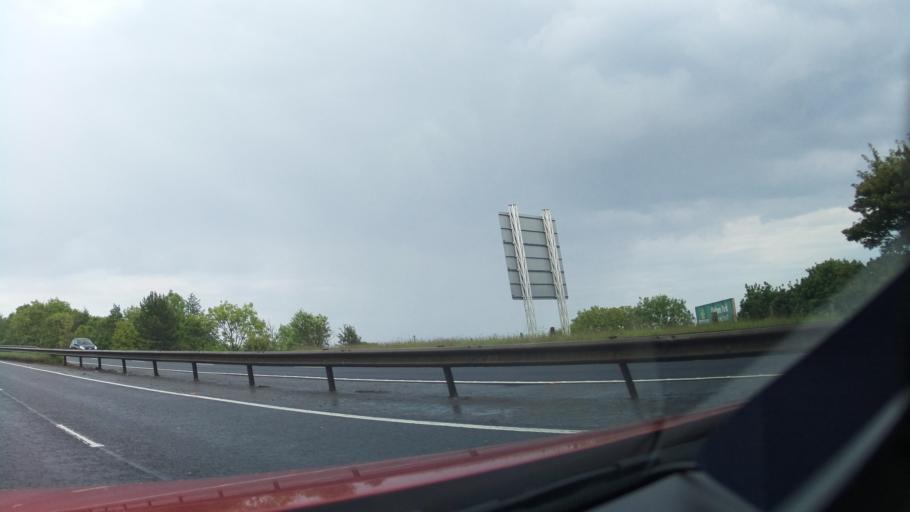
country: GB
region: England
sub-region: County Durham
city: Seaham
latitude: 54.8231
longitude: -1.3699
